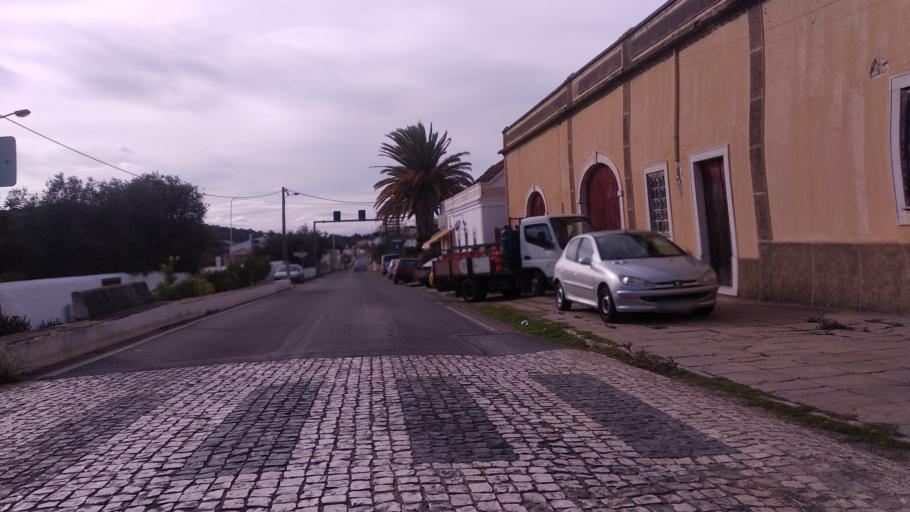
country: PT
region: Faro
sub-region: Sao Bras de Alportel
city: Sao Bras de Alportel
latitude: 37.1520
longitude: -7.9213
